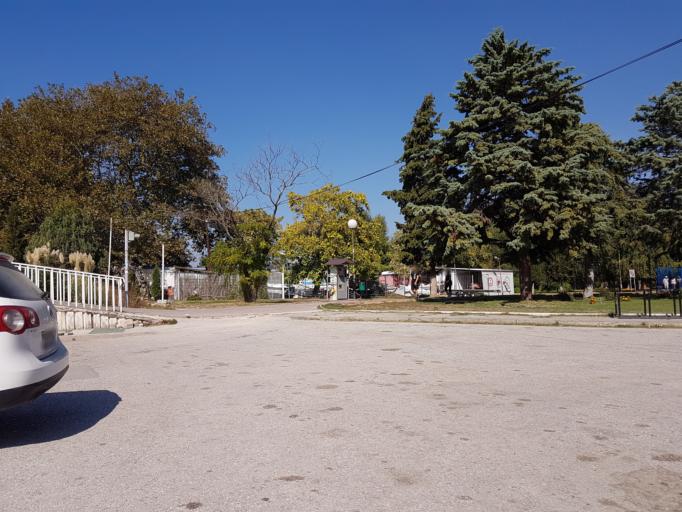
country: MK
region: Ohrid
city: Ohrid
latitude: 41.1041
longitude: 20.8082
